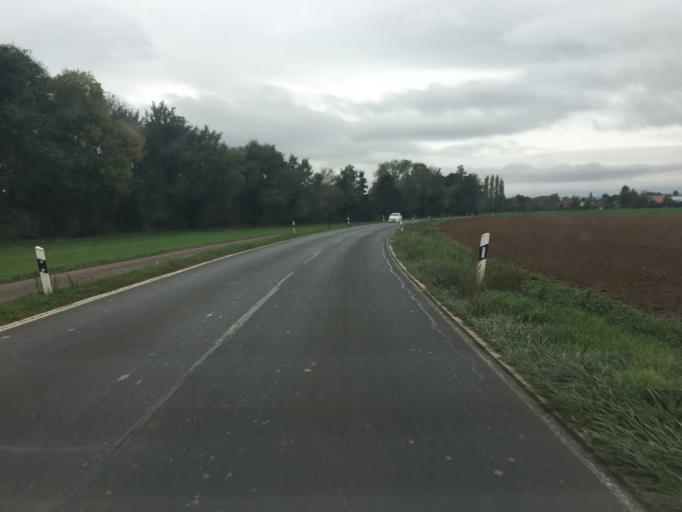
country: DE
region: North Rhine-Westphalia
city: Zulpich
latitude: 50.6764
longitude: 6.6763
